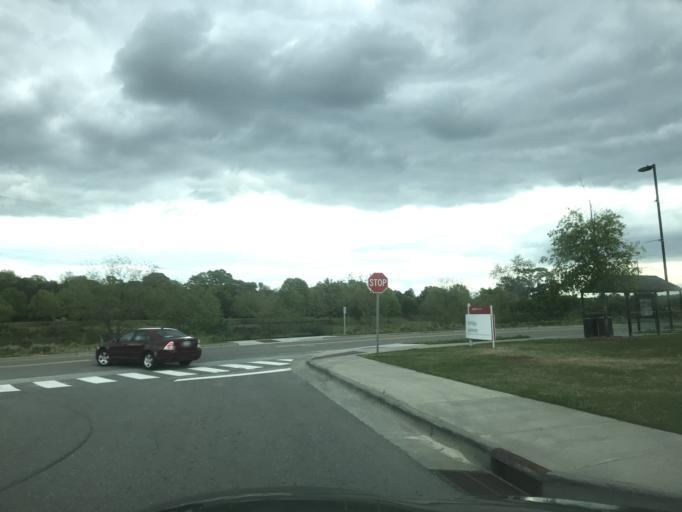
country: US
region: North Carolina
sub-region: Wake County
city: West Raleigh
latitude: 35.7693
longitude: -78.6722
